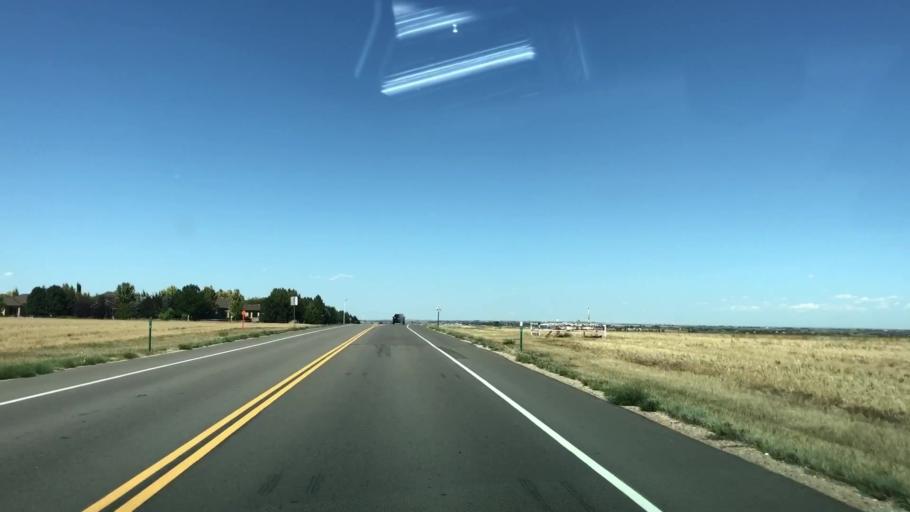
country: US
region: Colorado
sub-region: Weld County
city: Windsor
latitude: 40.4592
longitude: -104.9441
